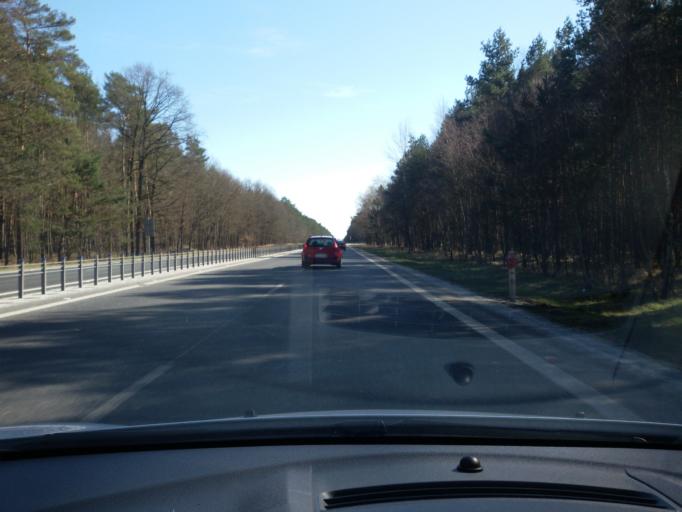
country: PL
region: Greater Poland Voivodeship
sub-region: Leszno
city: Leszno
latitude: 51.8180
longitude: 16.6185
